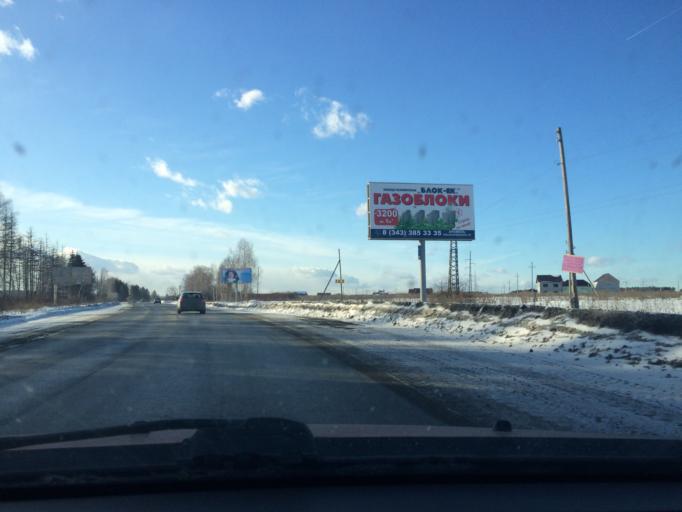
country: RU
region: Sverdlovsk
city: Aramil
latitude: 56.7733
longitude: 60.8551
